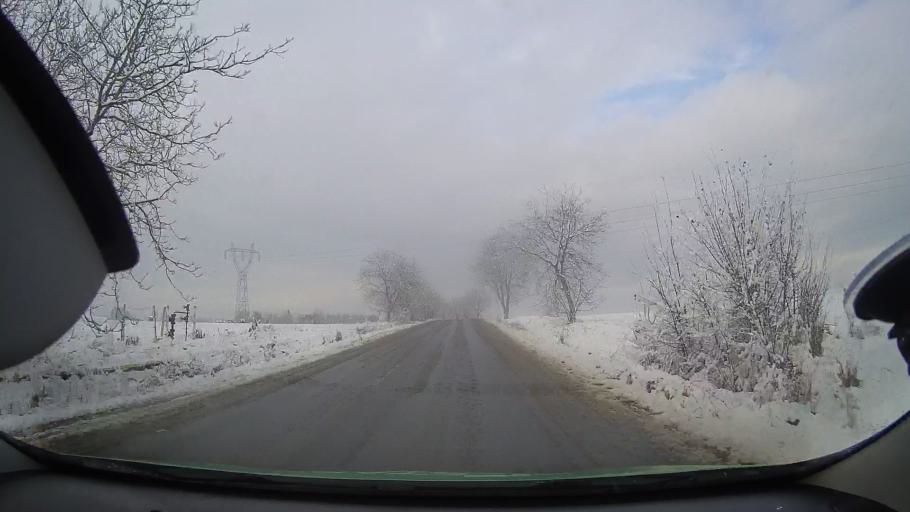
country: RO
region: Mures
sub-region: Comuna Atintis
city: Atintis
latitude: 46.4413
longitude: 24.0920
